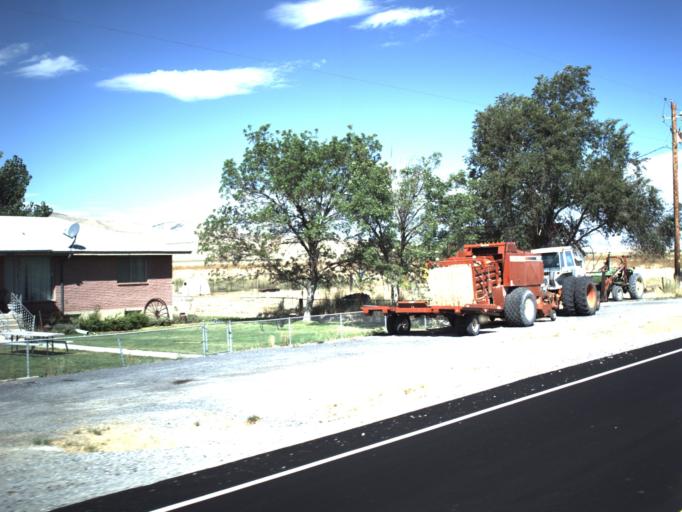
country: US
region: Utah
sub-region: Box Elder County
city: Garland
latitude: 41.7695
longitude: -112.4350
